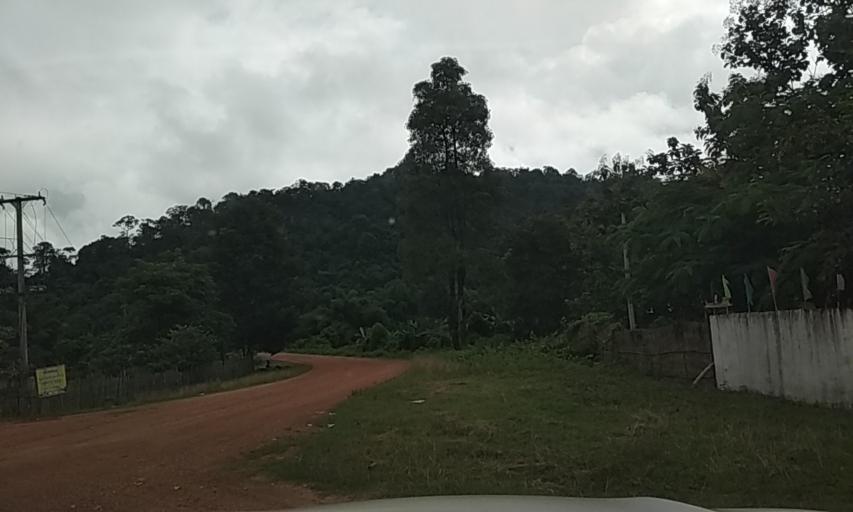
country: LA
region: Bolikhamxai
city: Bolikhan
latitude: 18.5571
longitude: 103.7419
